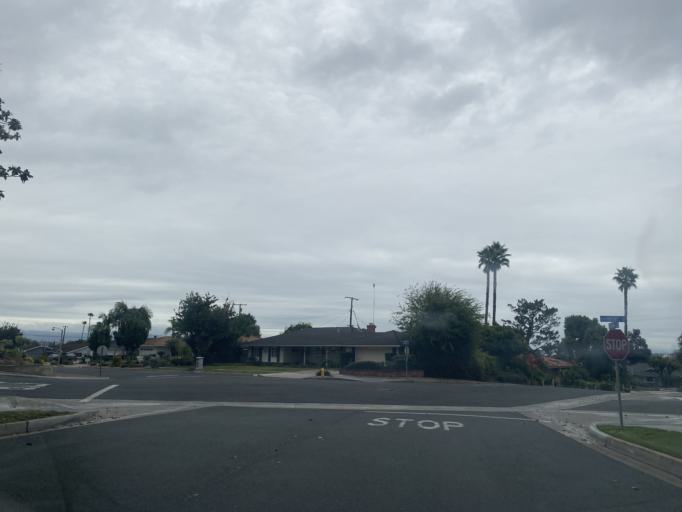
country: US
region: California
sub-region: Orange County
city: Fullerton
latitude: 33.8823
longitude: -117.9129
